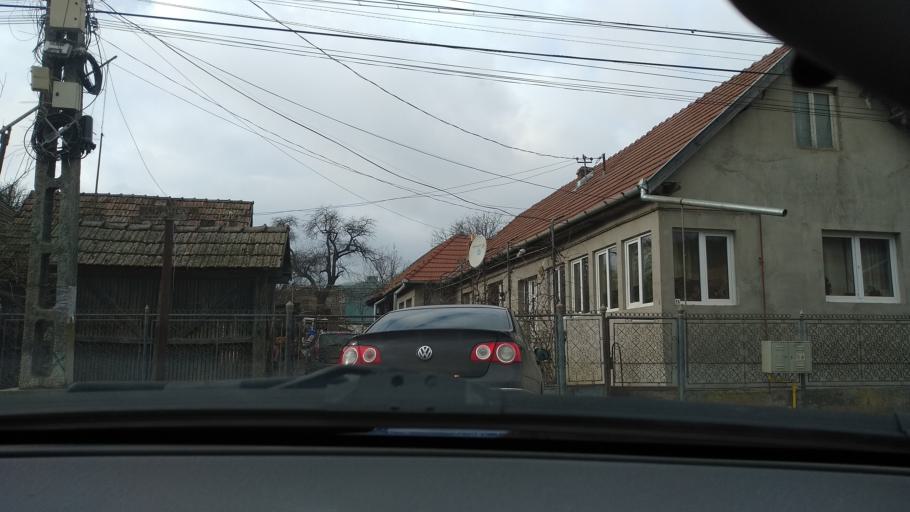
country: RO
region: Mures
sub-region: Comuna Panet
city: Panet
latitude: 46.5476
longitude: 24.4688
